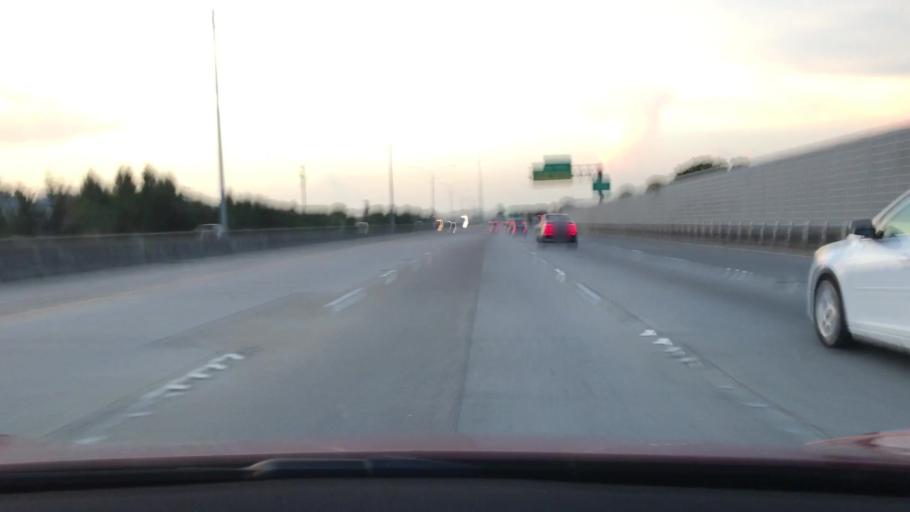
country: US
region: Louisiana
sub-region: Bossier Parish
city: Bossier City
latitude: 32.4723
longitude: -93.7552
